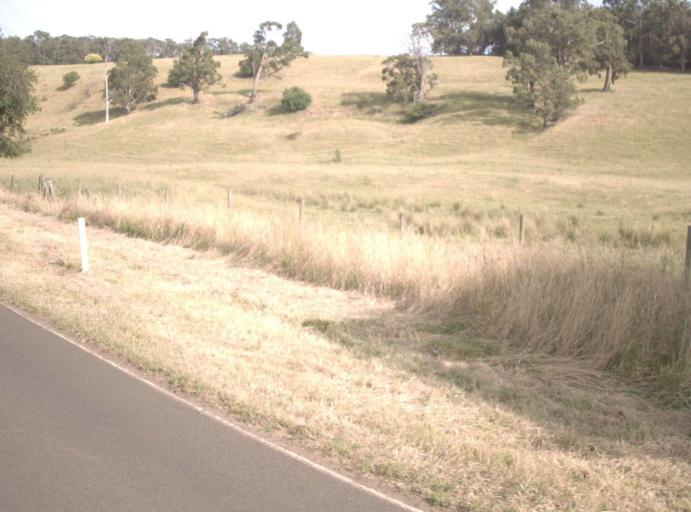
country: AU
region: Victoria
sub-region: Latrobe
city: Moe
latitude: -38.2761
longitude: 146.2867
